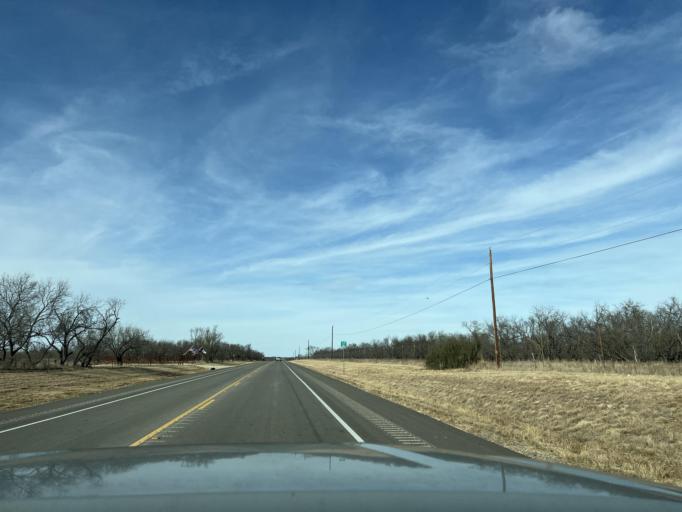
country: US
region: Texas
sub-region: Shackelford County
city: Albany
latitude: 32.6328
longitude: -99.2265
